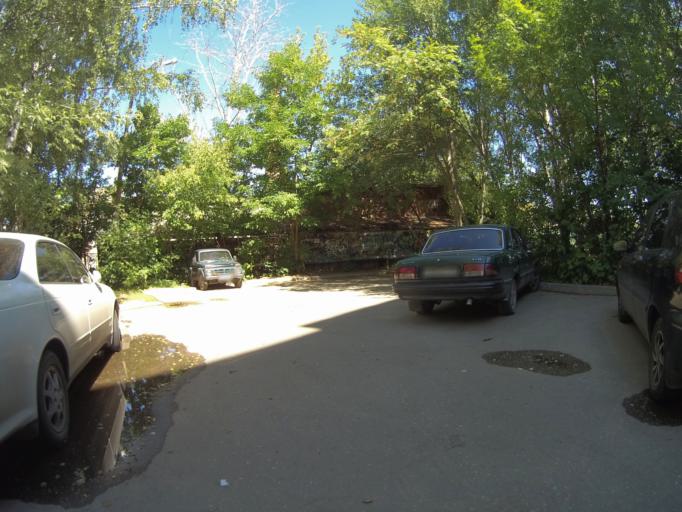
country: RU
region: Vladimir
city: Vladimir
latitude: 56.1296
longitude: 40.3612
